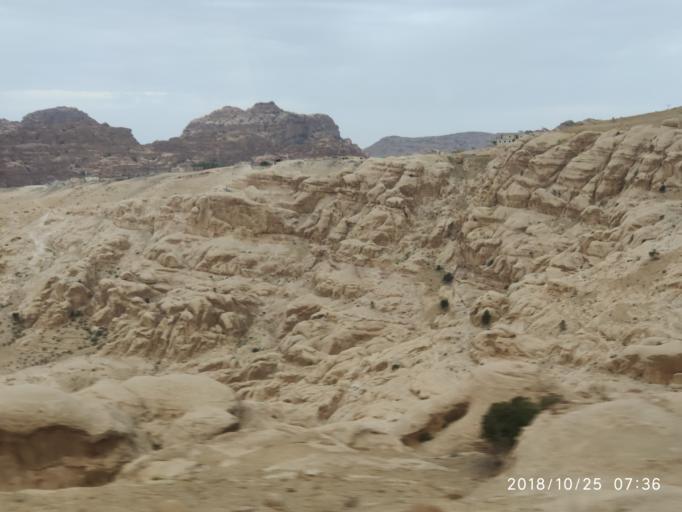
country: JO
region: Ma'an
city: Petra
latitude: 30.3395
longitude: 35.4672
